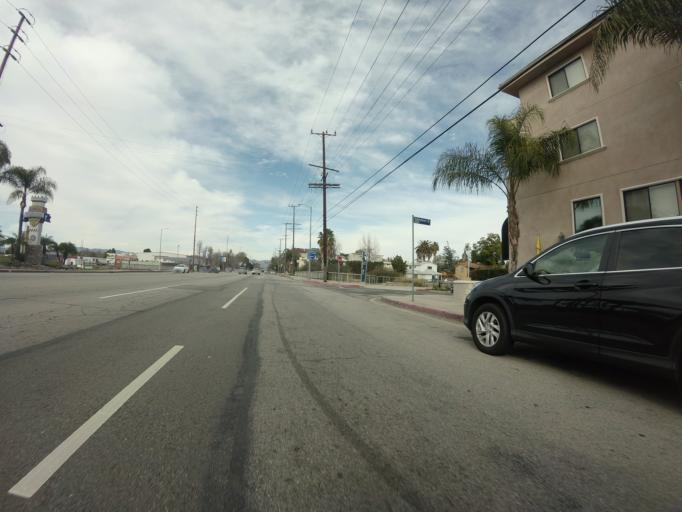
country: US
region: California
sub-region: Los Angeles County
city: Sherman Oaks
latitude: 34.1610
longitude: -118.4661
